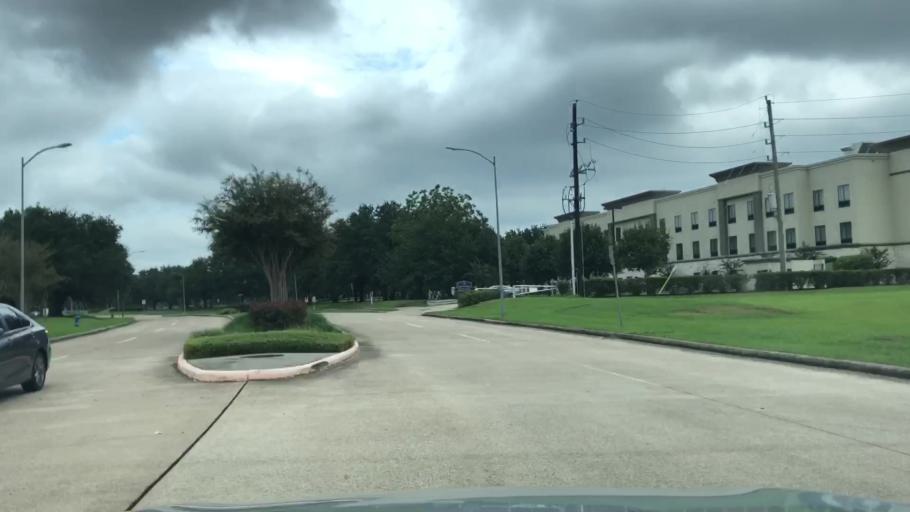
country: US
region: Texas
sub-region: Fort Bend County
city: Meadows Place
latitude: 29.7065
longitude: -95.5599
